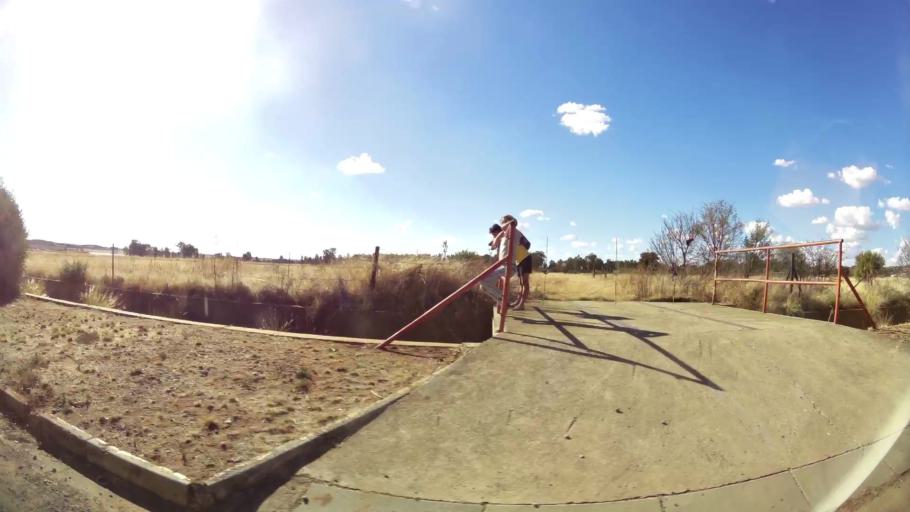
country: ZA
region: North-West
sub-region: Dr Kenneth Kaunda District Municipality
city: Klerksdorp
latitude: -26.8176
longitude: 26.6607
